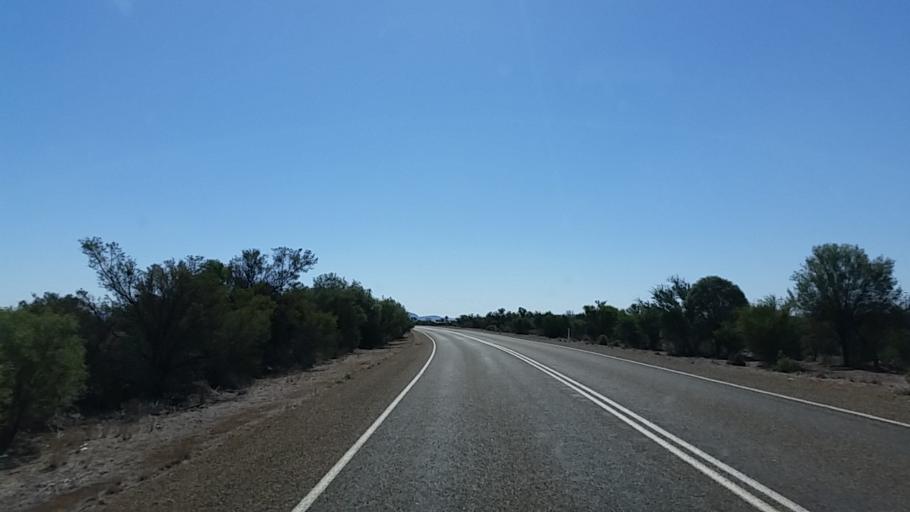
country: AU
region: South Australia
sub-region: Flinders Ranges
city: Quorn
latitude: -32.0771
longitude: 138.5017
